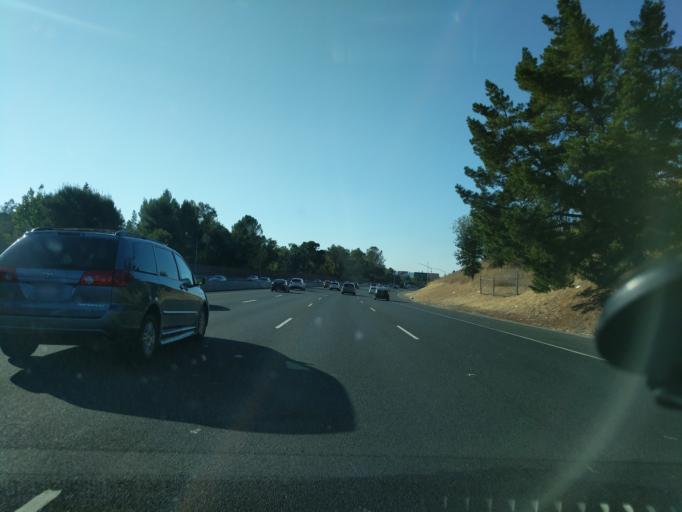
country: US
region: California
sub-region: Contra Costa County
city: Alamo
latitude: 37.8461
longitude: -122.0258
